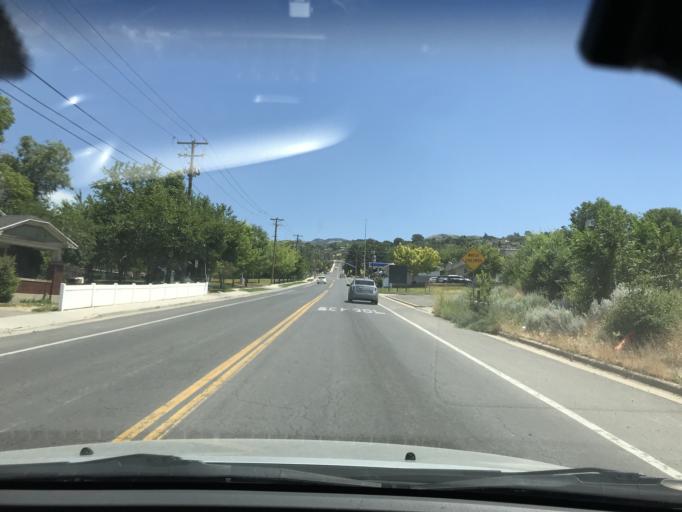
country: US
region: Utah
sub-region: Davis County
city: North Salt Lake
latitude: 40.8418
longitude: -111.9083
